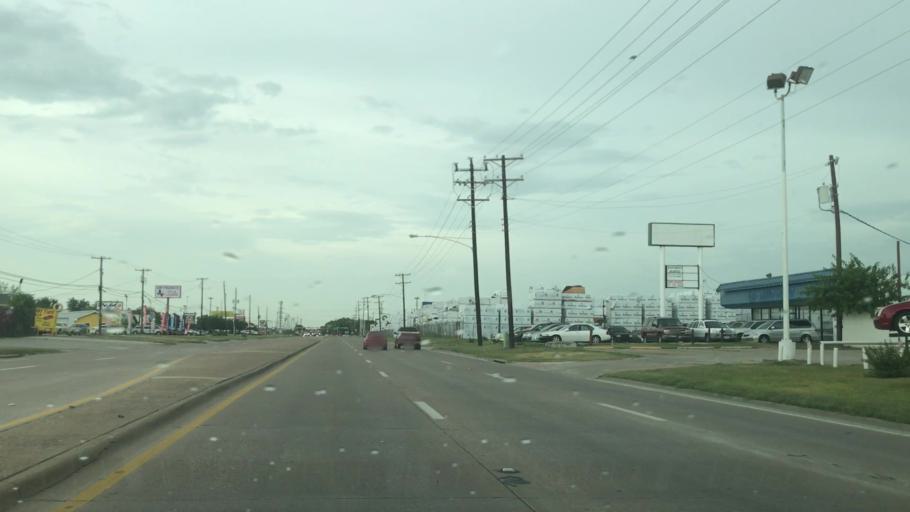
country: US
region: Texas
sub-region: Dallas County
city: Garland
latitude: 32.8592
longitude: -96.6741
